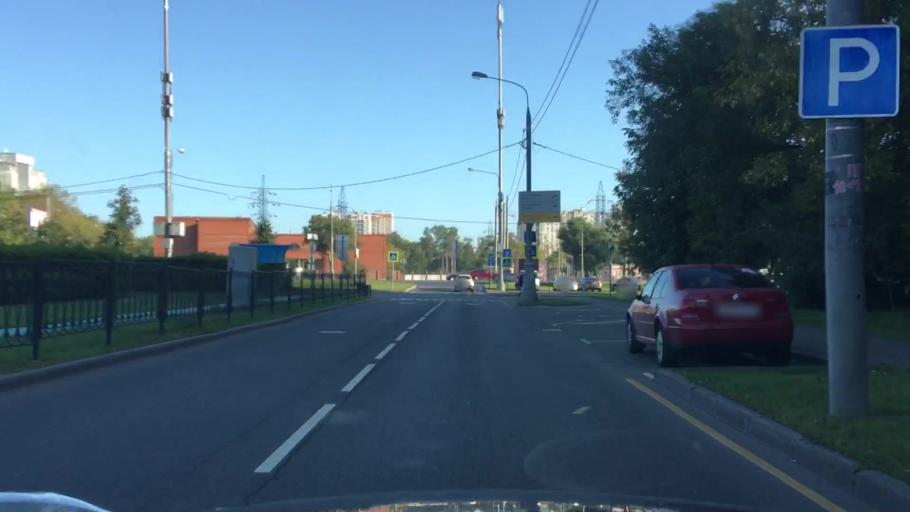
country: RU
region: Moscow
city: Davydkovo
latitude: 55.7250
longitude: 37.4613
